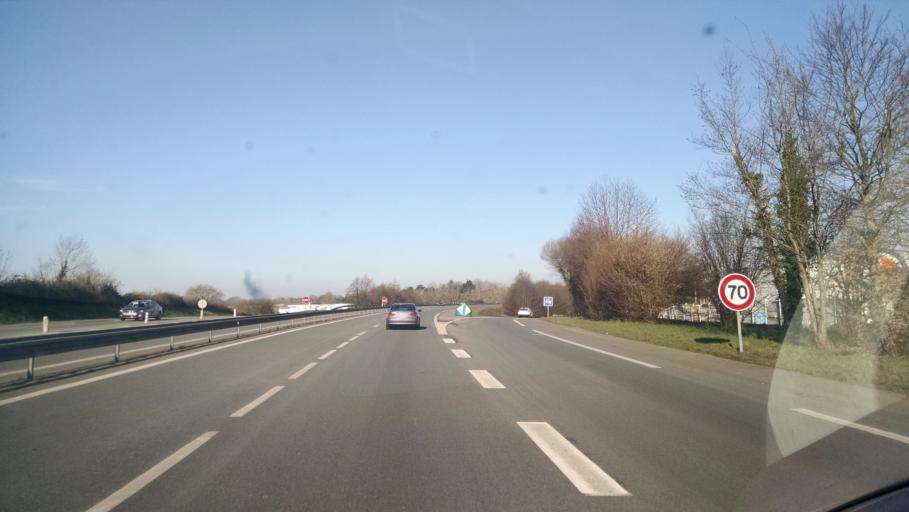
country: FR
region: Brittany
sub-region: Departement du Morbihan
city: Auray
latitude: 47.6609
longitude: -3.0074
